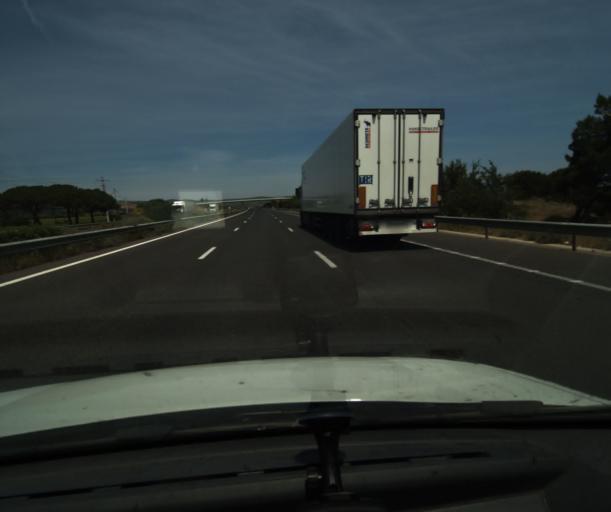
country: FR
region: Languedoc-Roussillon
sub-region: Departement des Pyrenees-Orientales
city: Salses-le-Chateau
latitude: 42.8129
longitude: 2.9058
